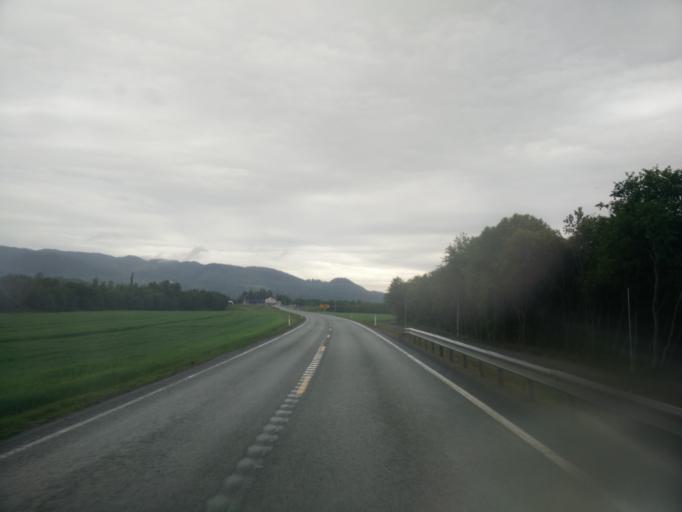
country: NO
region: Sor-Trondelag
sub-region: Orkdal
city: Orkanger
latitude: 63.2709
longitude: 9.8045
